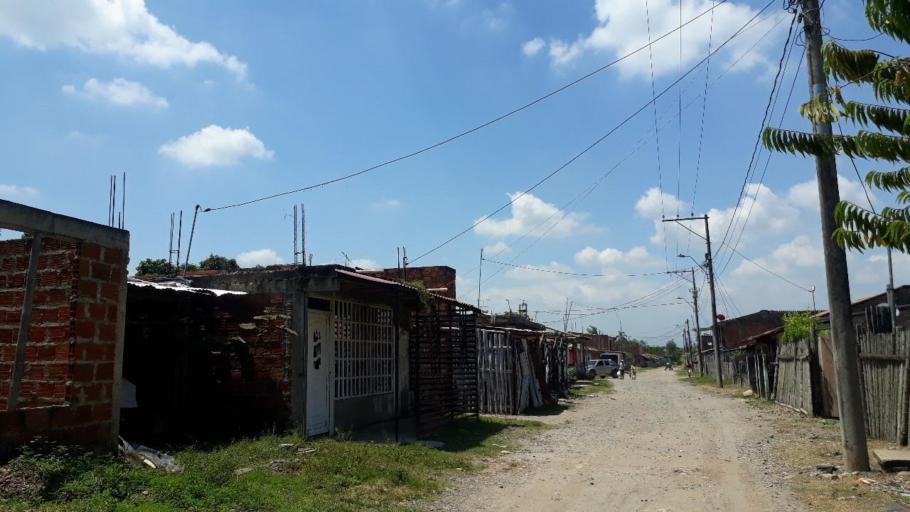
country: CO
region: Valle del Cauca
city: Jamundi
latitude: 3.1331
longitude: -76.5439
